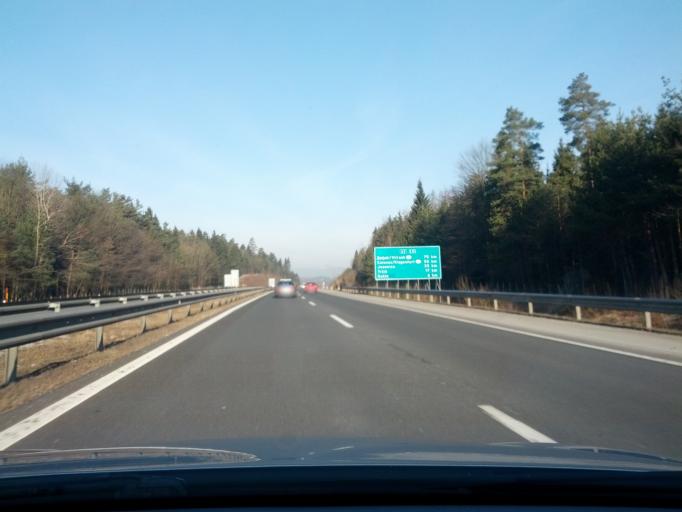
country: SI
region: Naklo
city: Naklo
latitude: 46.2679
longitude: 14.3349
